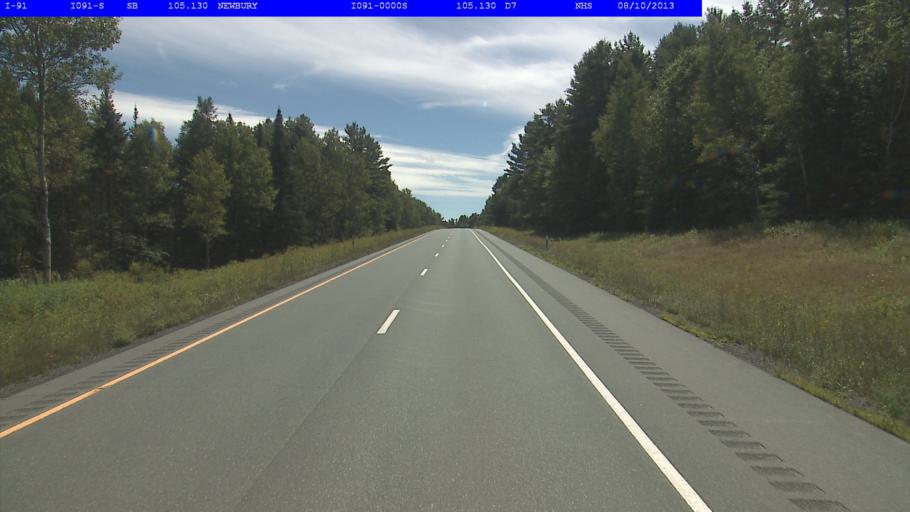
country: US
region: New Hampshire
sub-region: Grafton County
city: Haverhill
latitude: 44.0878
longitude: -72.1128
